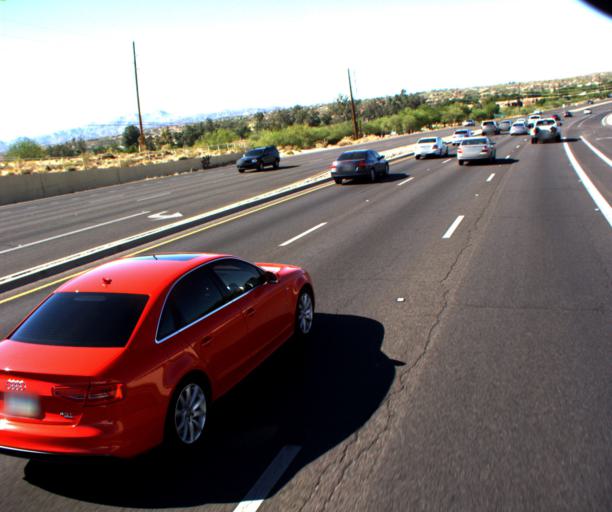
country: US
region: Arizona
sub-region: Pima County
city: Oro Valley
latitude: 32.3892
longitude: -110.9641
